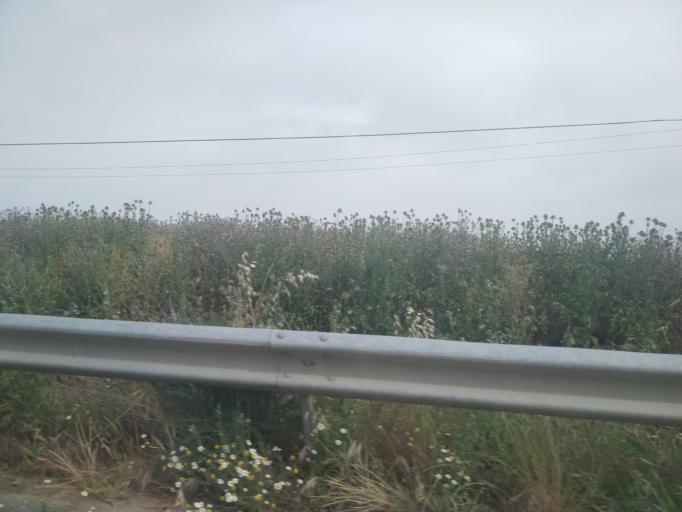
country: ES
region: Castille-La Mancha
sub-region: Province of Toledo
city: Guadamur
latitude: 39.8014
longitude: -4.1378
